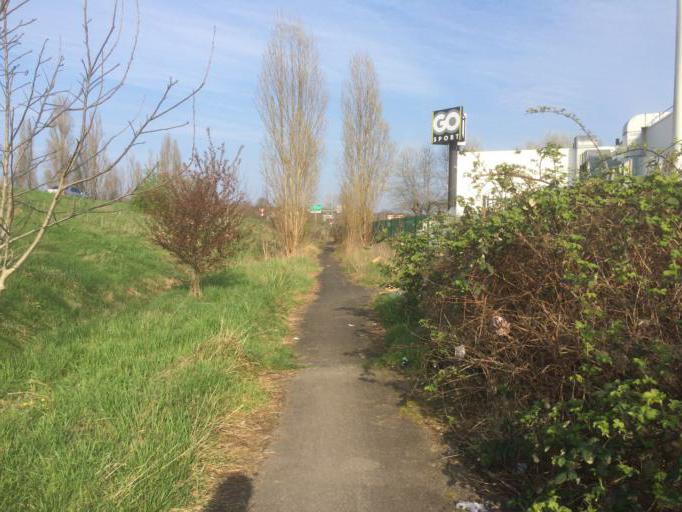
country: FR
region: Ile-de-France
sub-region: Departement de l'Essonne
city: Fleury-Merogis
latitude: 48.6260
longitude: 2.3432
